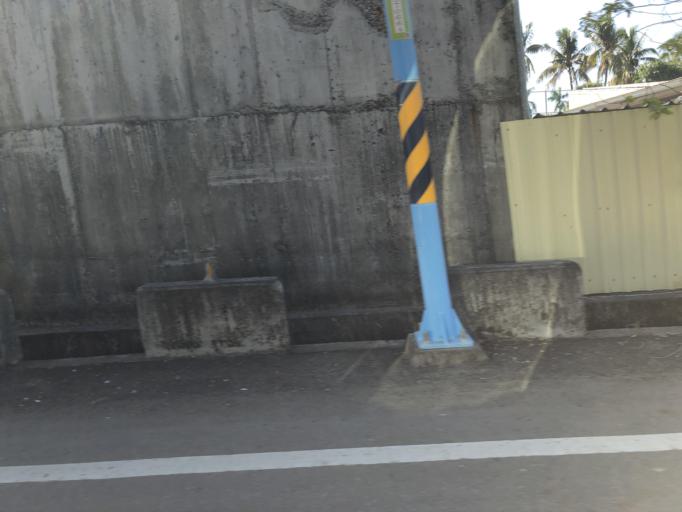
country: TW
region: Taiwan
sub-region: Tainan
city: Tainan
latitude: 23.0377
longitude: 120.3389
